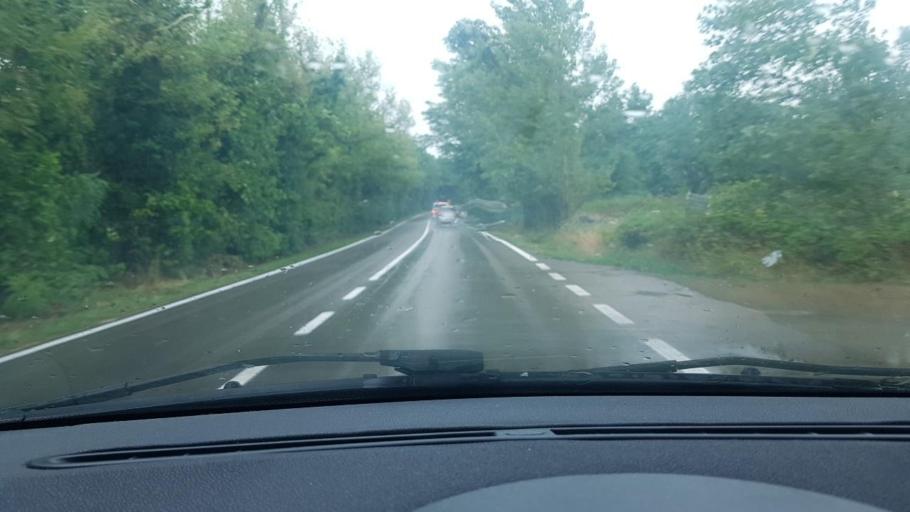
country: IT
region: Veneto
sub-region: Provincia di Verona
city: Garda
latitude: 45.5983
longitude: 10.7176
